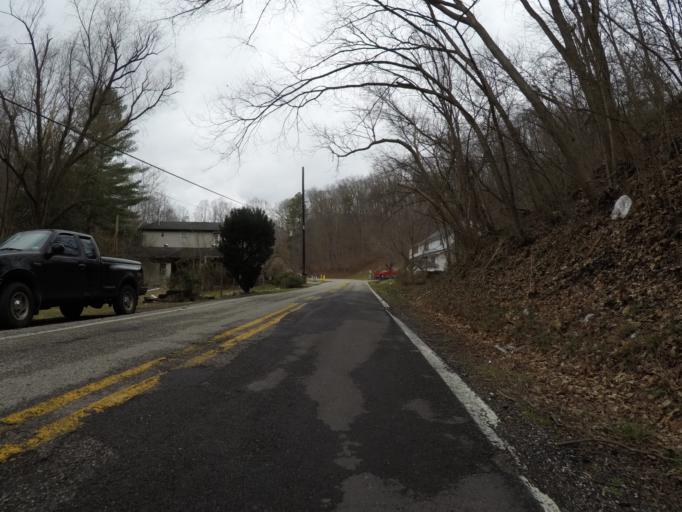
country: US
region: West Virginia
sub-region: Cabell County
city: Barboursville
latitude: 38.4497
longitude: -82.2583
